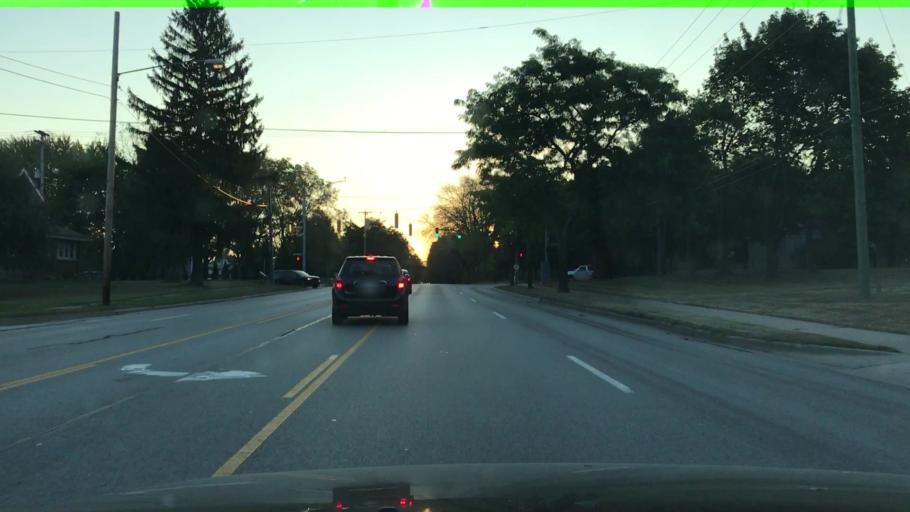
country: US
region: Michigan
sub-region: Kent County
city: East Grand Rapids
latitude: 42.9843
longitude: -85.6017
